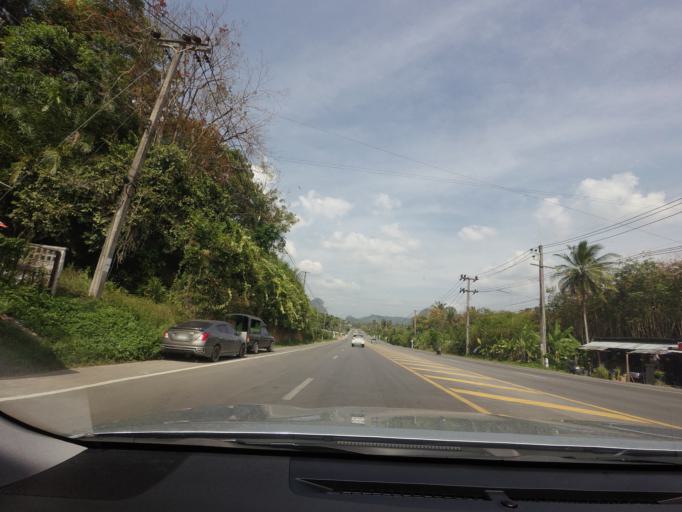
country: TH
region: Phangnga
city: Ban Ao Nang
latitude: 8.0519
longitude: 98.7734
